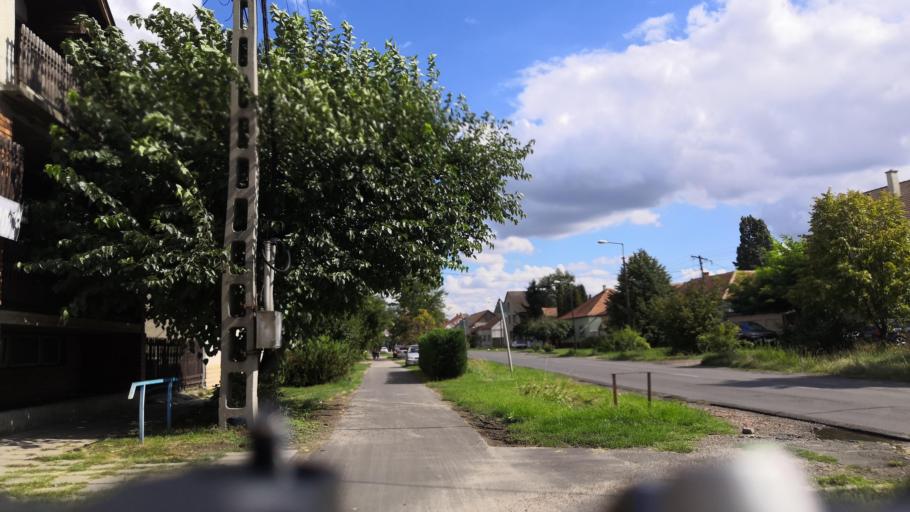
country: HU
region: Csongrad
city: Domaszek
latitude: 46.2768
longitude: 20.0561
